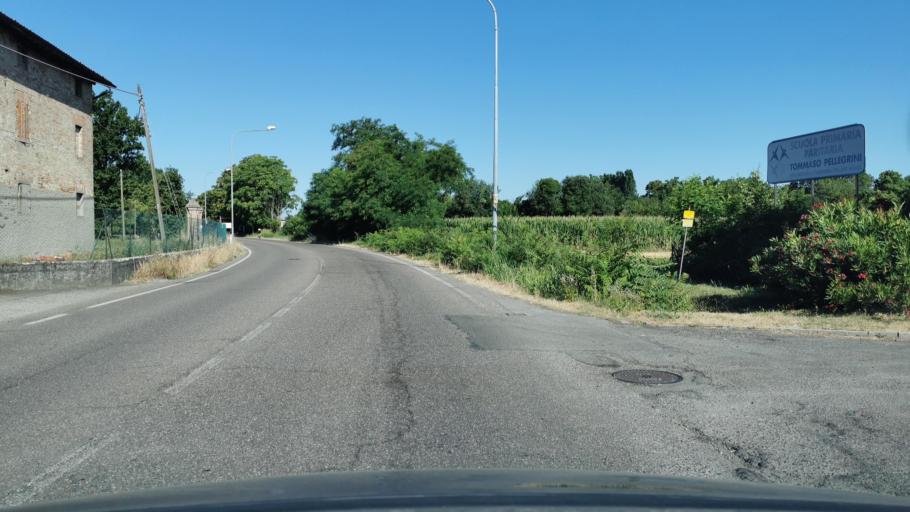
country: IT
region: Emilia-Romagna
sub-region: Provincia di Modena
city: Modena
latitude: 44.6191
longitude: 10.9007
